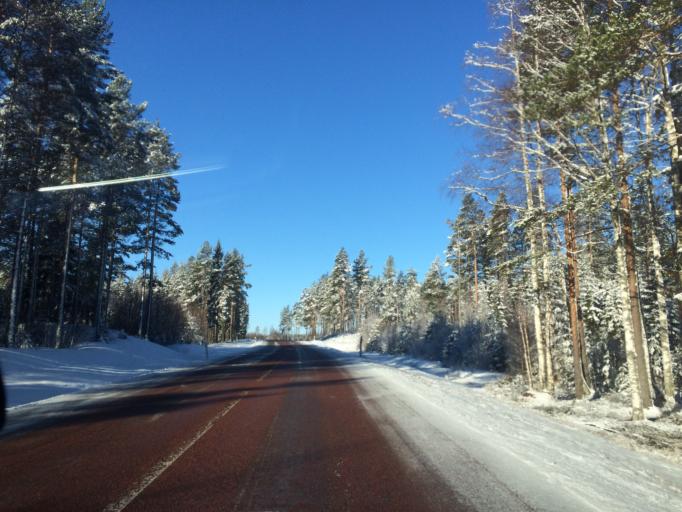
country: SE
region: Dalarna
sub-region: Mora Kommun
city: Mora
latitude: 60.8534
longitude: 14.2496
